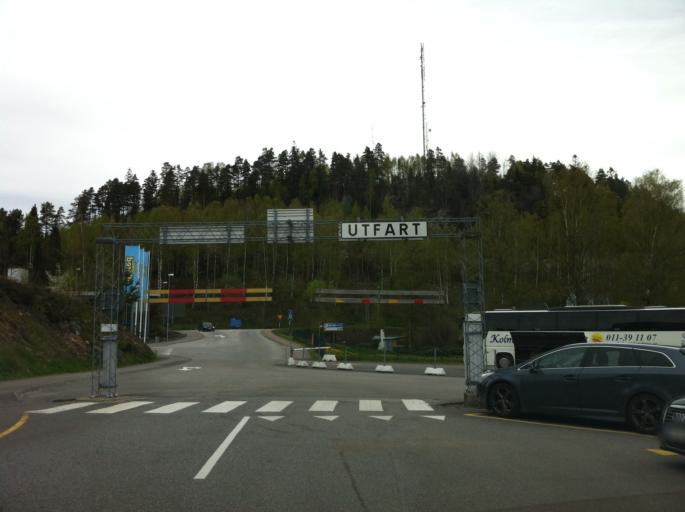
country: SE
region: Halland
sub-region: Falkenbergs Kommun
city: Falkenberg
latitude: 57.1365
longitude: 12.7105
